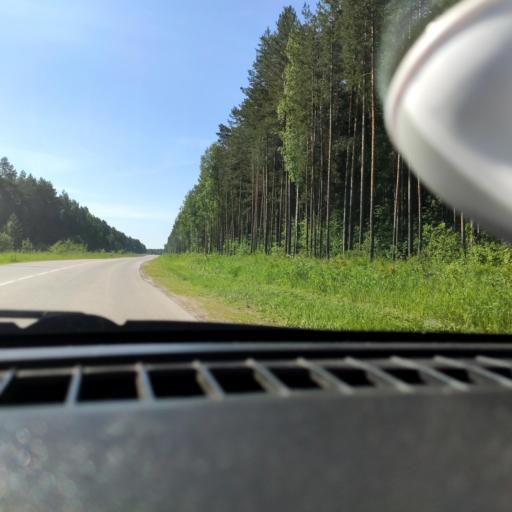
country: RU
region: Perm
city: Overyata
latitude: 58.0076
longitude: 55.8757
